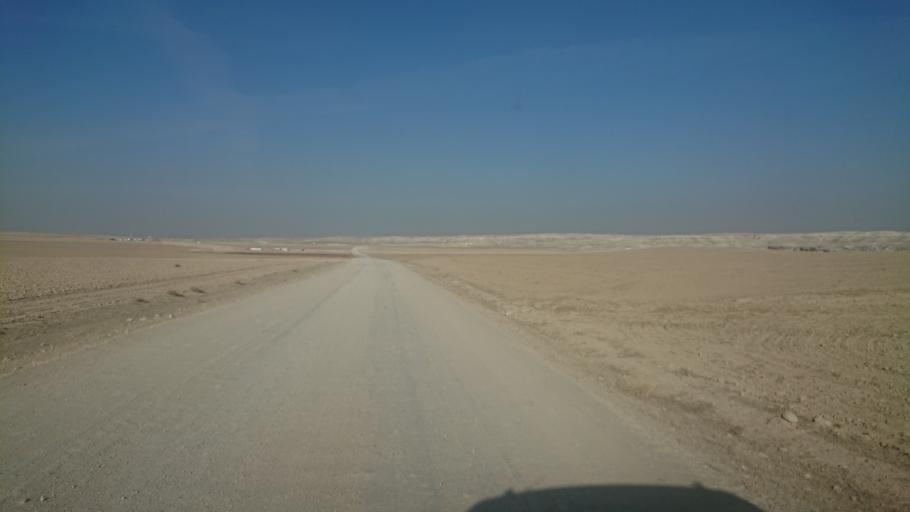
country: TR
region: Aksaray
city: Sultanhani
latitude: 38.0621
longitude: 33.6149
